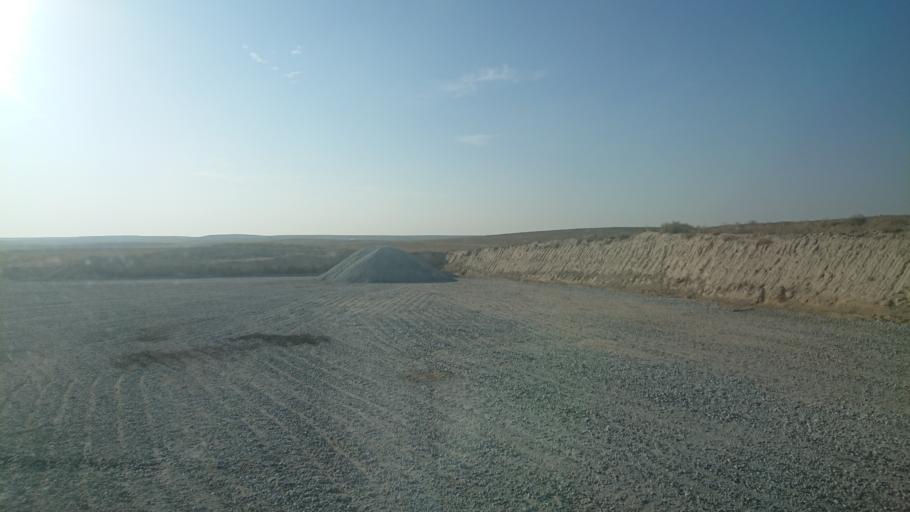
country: TR
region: Aksaray
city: Sultanhani
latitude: 38.0863
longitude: 33.6207
